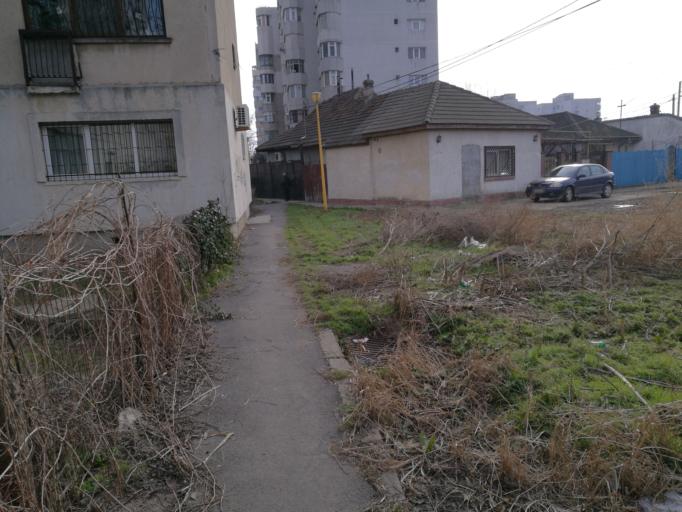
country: RO
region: Constanta
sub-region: Municipiul Constanta
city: Constanta
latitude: 44.1729
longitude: 28.6095
